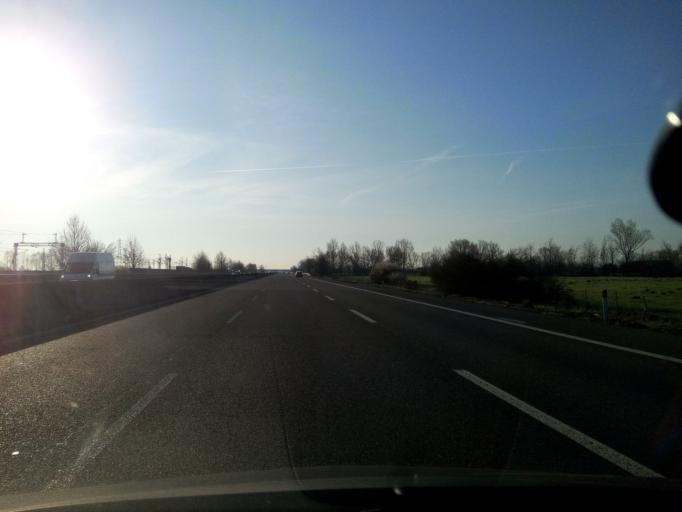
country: IT
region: Emilia-Romagna
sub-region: Provincia di Piacenza
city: Alseno
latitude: 44.9138
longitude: 10.0123
